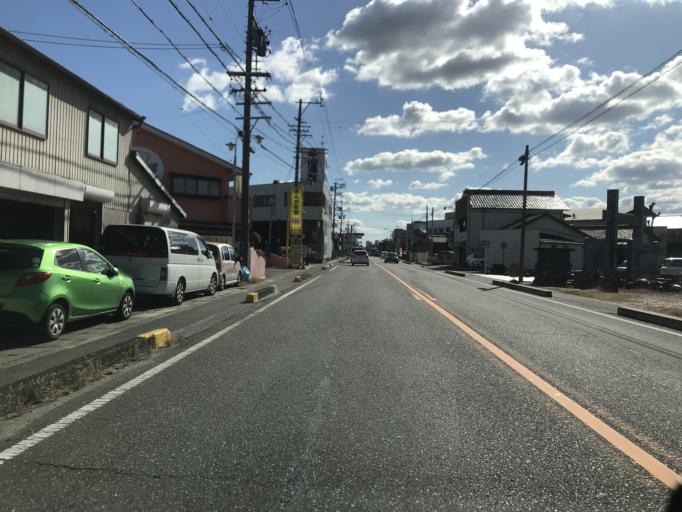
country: JP
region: Aichi
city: Nagoya-shi
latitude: 35.2167
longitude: 136.8464
